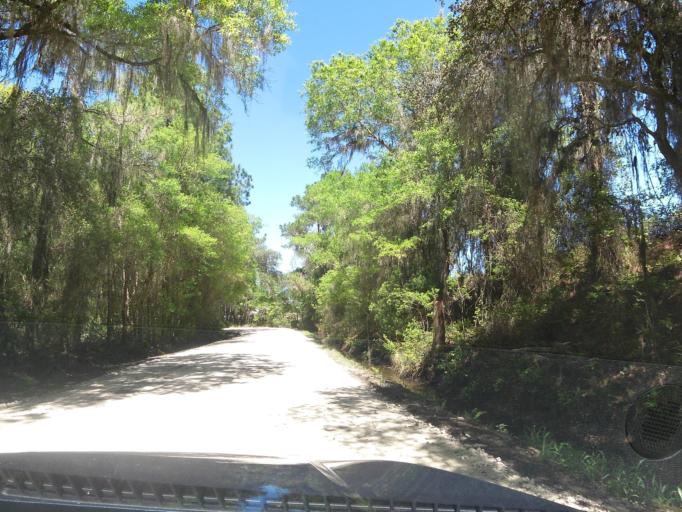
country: US
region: Florida
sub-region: Bradford County
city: Starke
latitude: 30.0514
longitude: -82.0533
